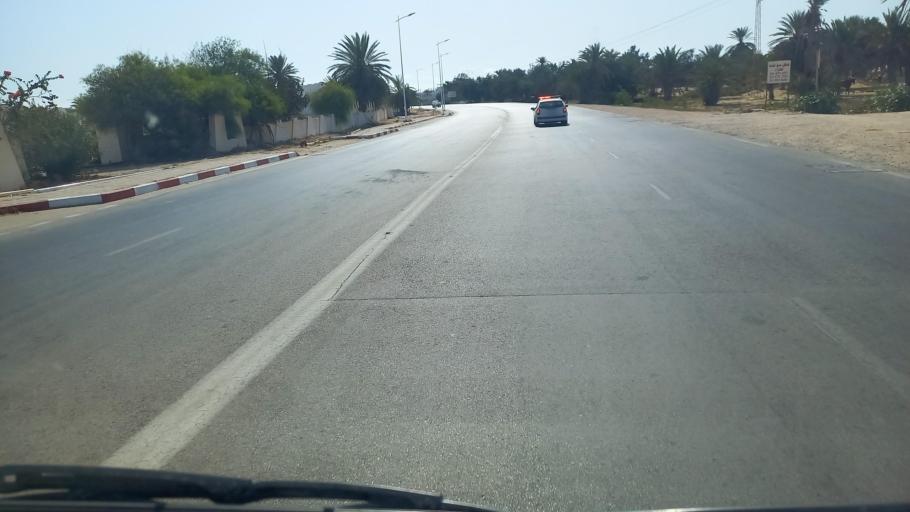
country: TN
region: Madanin
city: Midoun
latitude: 33.8376
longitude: 10.9958
